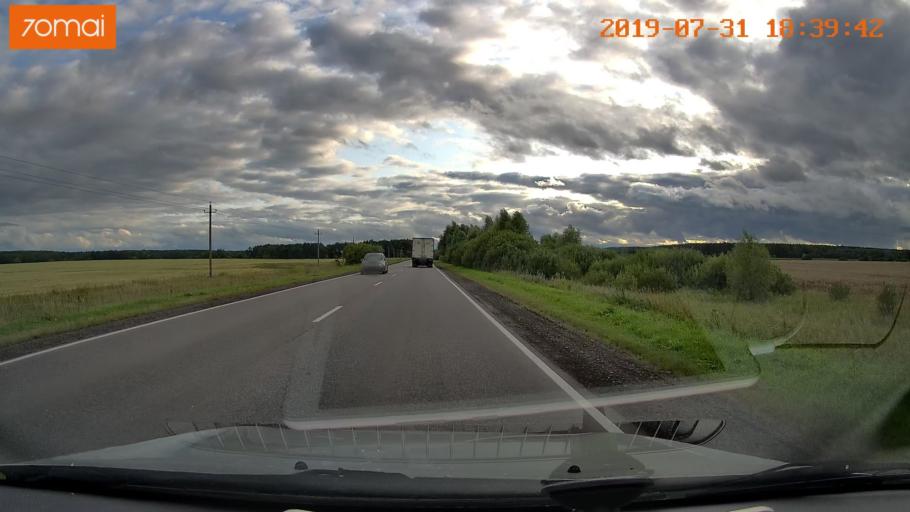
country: RU
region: Moskovskaya
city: Voskresensk
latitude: 55.2655
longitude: 38.6416
